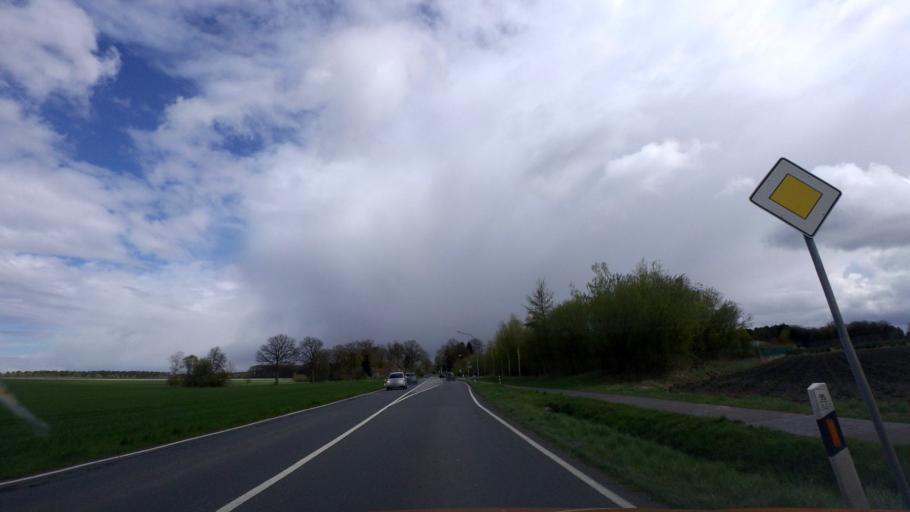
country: DE
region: Lower Saxony
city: Schneverdingen
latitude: 53.0823
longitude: 9.8654
